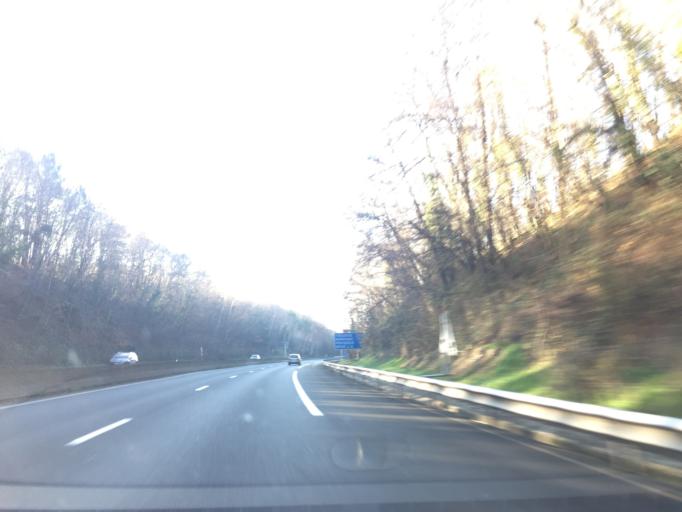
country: FR
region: Limousin
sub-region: Departement de la Correze
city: Donzenac
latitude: 45.2466
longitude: 1.5253
